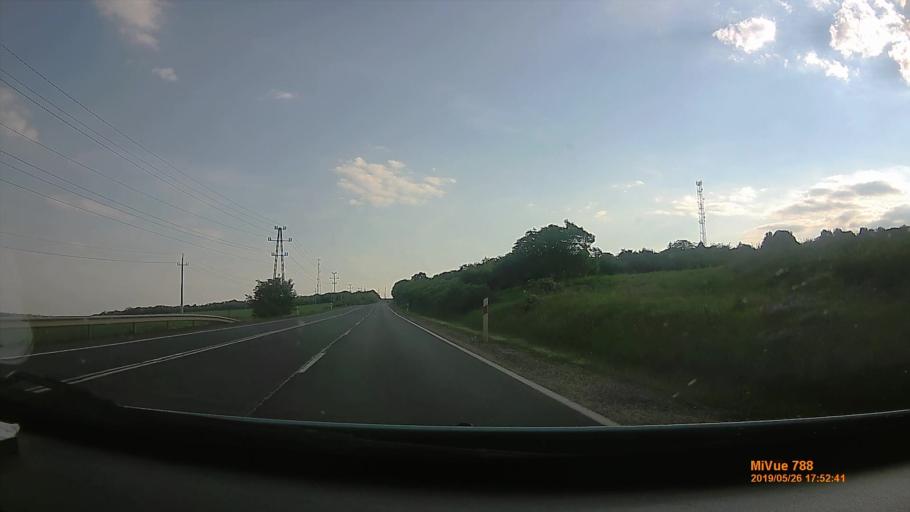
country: HU
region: Borsod-Abauj-Zemplen
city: Onga
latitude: 48.1616
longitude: 20.9044
